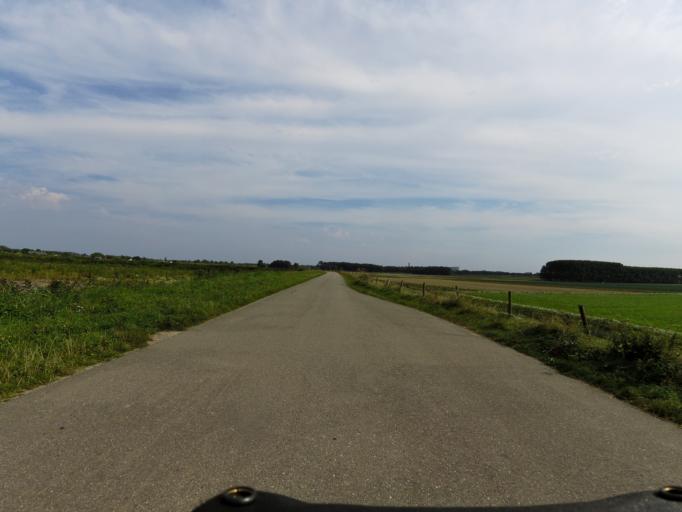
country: NL
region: South Holland
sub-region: Gemeente Zwijndrecht
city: Heerjansdam
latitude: 51.8212
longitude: 4.5421
